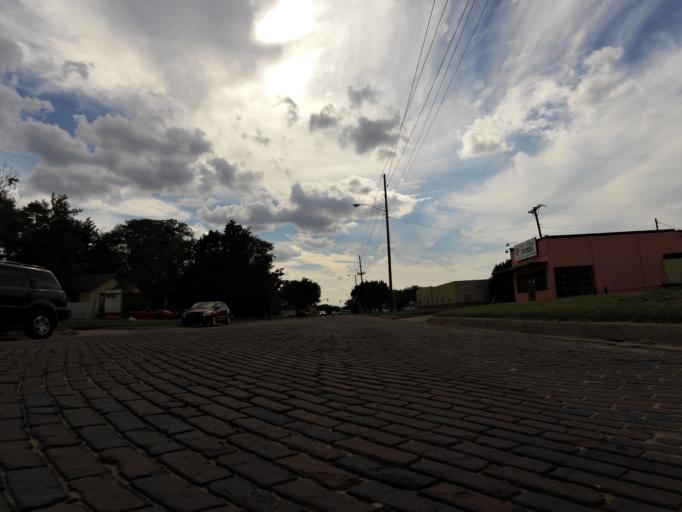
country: US
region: Kansas
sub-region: Sedgwick County
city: Wichita
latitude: 37.7011
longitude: -97.3066
